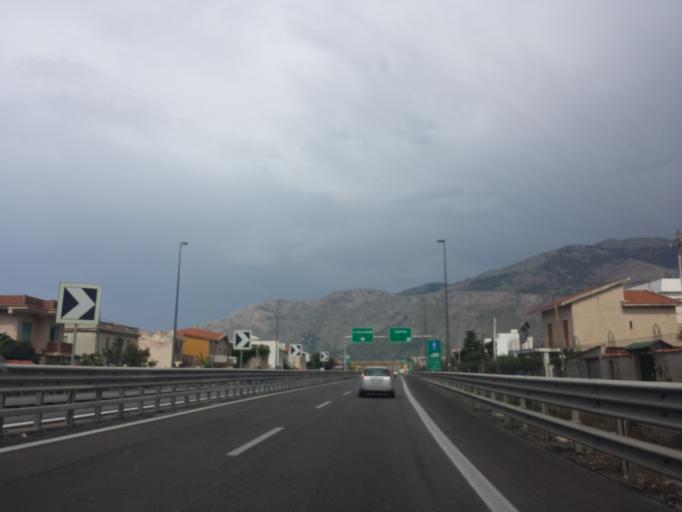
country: IT
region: Sicily
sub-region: Palermo
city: Capaci
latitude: 38.1739
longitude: 13.2098
